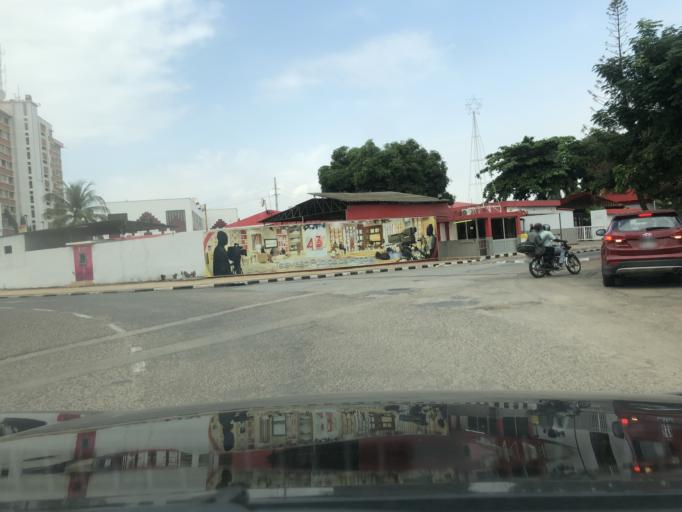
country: AO
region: Luanda
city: Luanda
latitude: -8.8299
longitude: 13.2398
